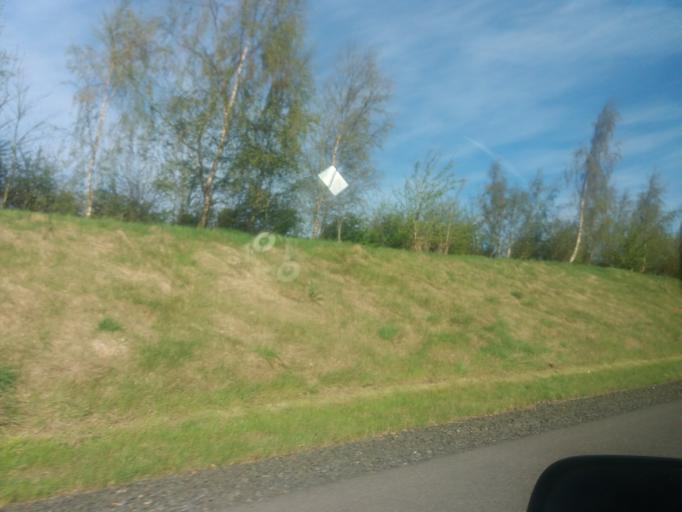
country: IE
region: Leinster
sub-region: An Mhi
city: Navan
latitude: 53.6575
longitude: -6.7562
